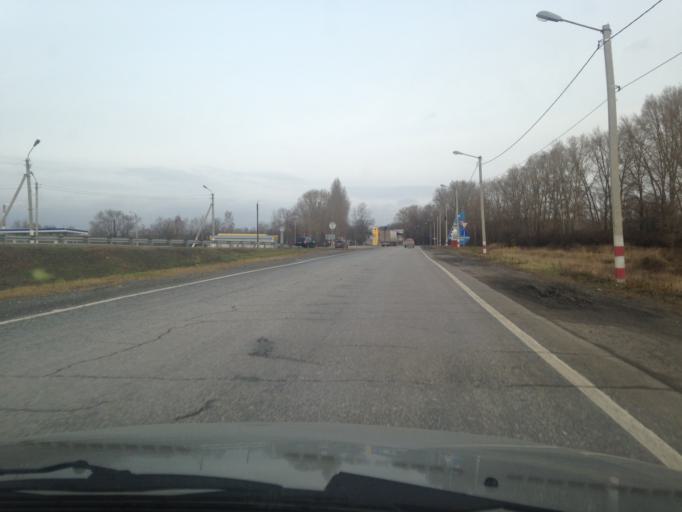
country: RU
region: Ulyanovsk
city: Novoul'yanovsk
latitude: 54.2115
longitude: 48.2968
